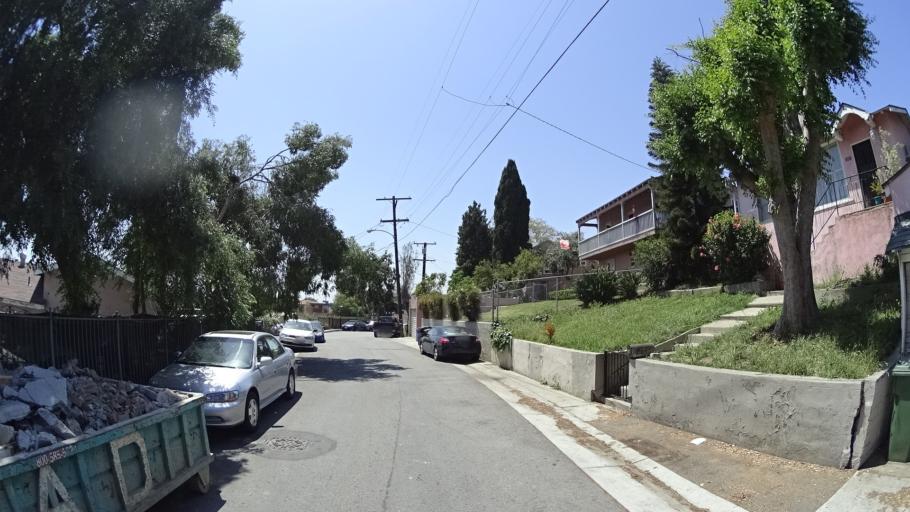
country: US
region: California
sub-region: Los Angeles County
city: Belvedere
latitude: 34.0530
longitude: -118.1815
